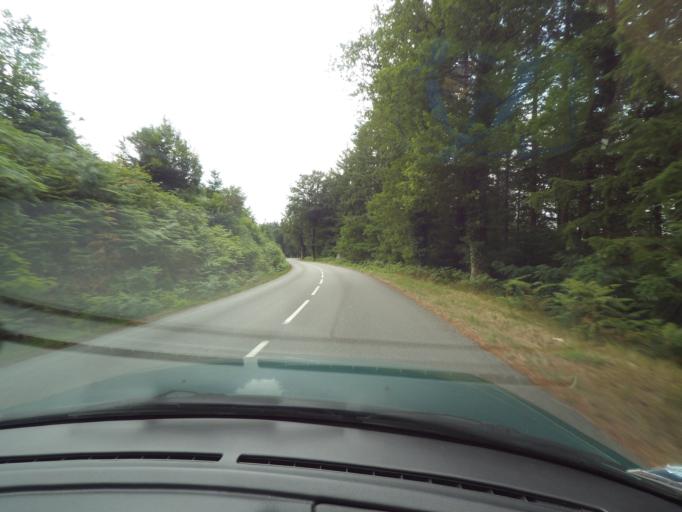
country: FR
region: Limousin
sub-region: Departement de la Haute-Vienne
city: Eymoutiers
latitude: 45.7256
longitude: 1.7871
